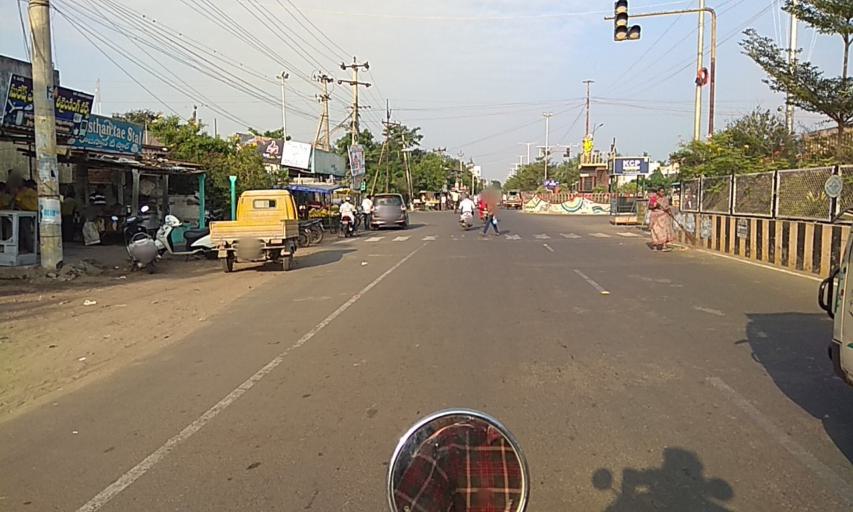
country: IN
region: Andhra Pradesh
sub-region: Krishna
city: Machilipatnam
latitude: 16.1929
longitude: 81.1425
